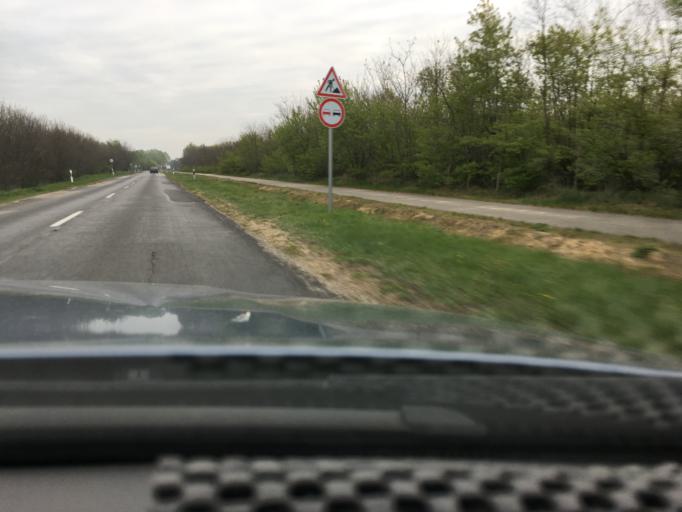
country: HU
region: Hajdu-Bihar
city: Hajdusamson
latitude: 47.6275
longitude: 21.7894
